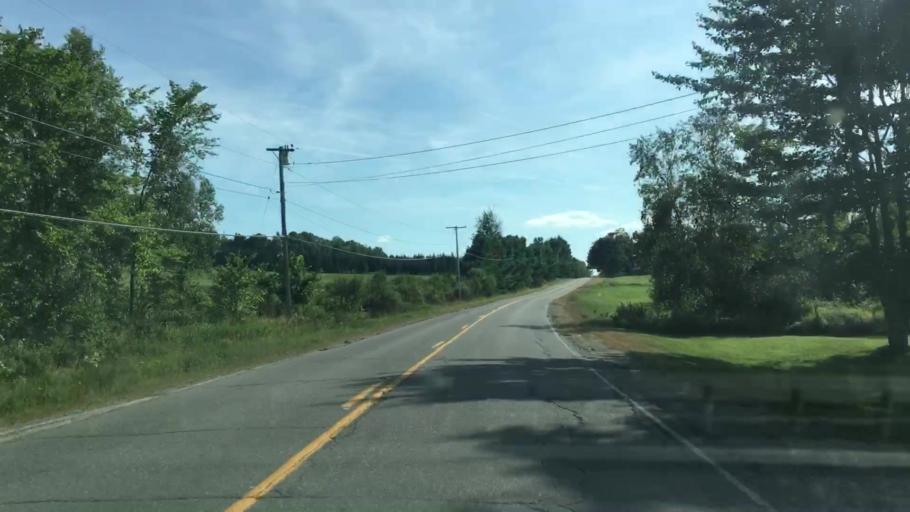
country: US
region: Maine
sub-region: Penobscot County
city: Lincoln
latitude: 45.3215
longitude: -68.5335
